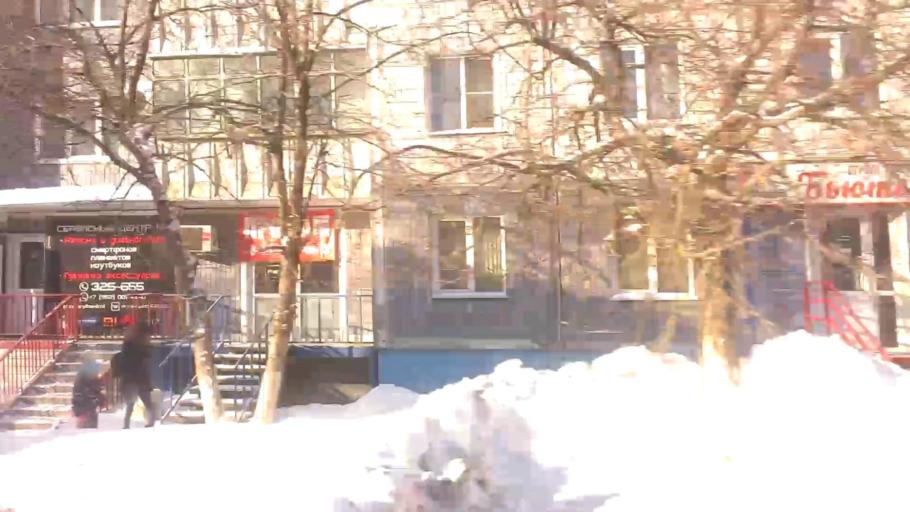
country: RU
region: Altai Krai
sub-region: Gorod Barnaulskiy
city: Barnaul
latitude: 53.3466
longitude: 83.7589
